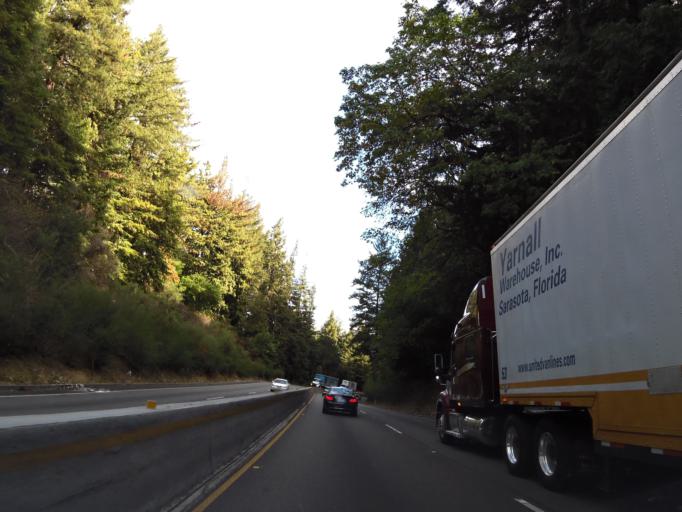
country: US
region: California
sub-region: Santa Clara County
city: Lexington Hills
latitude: 37.1617
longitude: -121.9891
